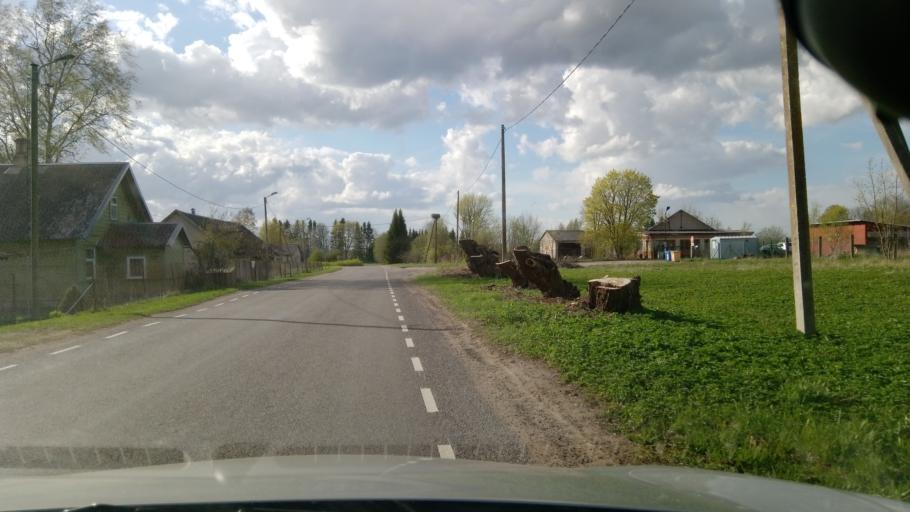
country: EE
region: Jaervamaa
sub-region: Jaerva-Jaani vald
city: Jarva-Jaani
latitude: 58.9454
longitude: 25.8322
